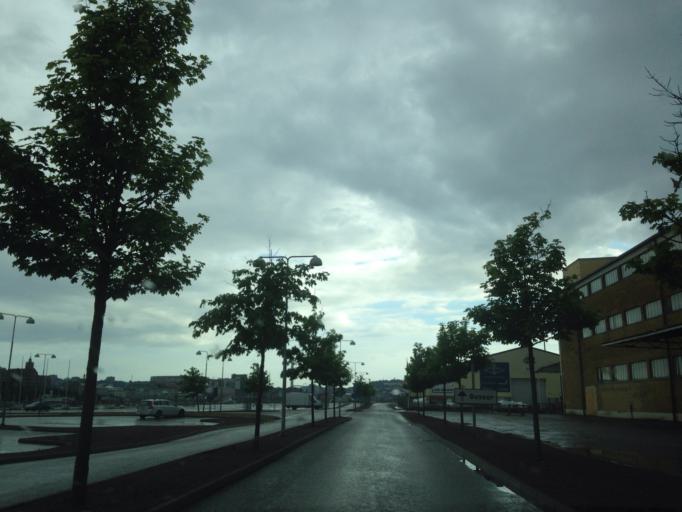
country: SE
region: Vaestra Goetaland
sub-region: Goteborg
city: Goeteborg
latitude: 57.7161
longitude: 11.9597
